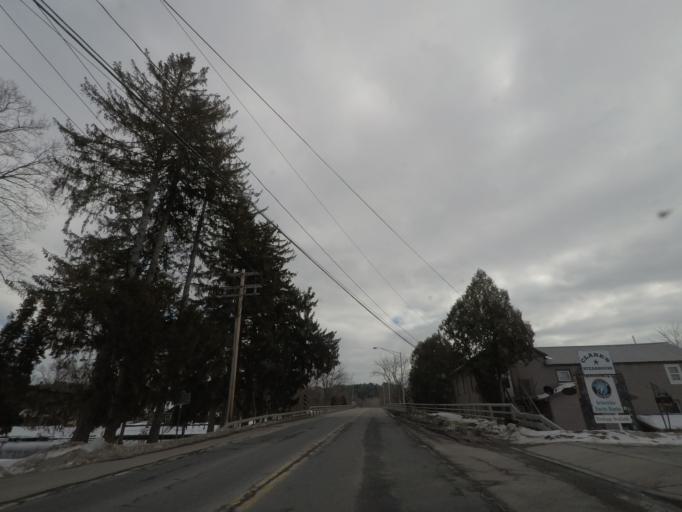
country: US
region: New York
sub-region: Saratoga County
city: Schuylerville
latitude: 43.0989
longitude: -73.5767
